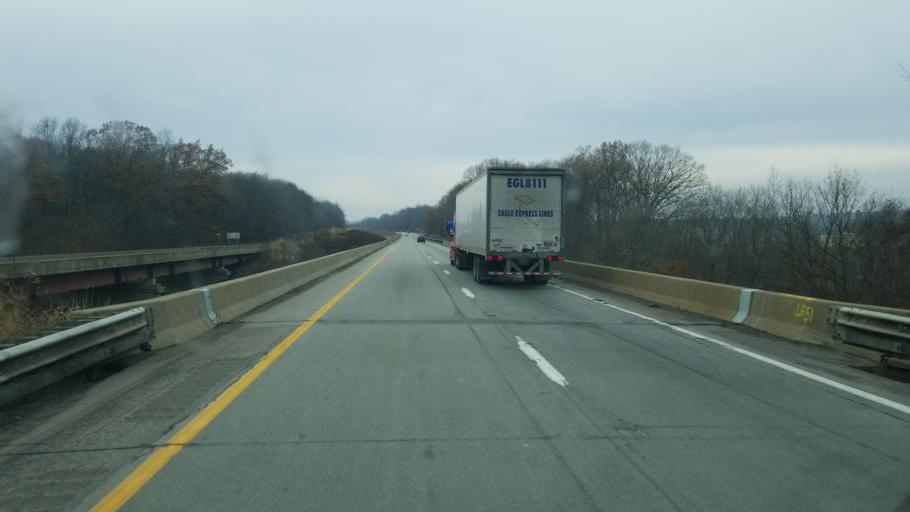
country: US
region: Pennsylvania
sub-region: Mercer County
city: Mercer
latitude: 41.1941
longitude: -80.2217
